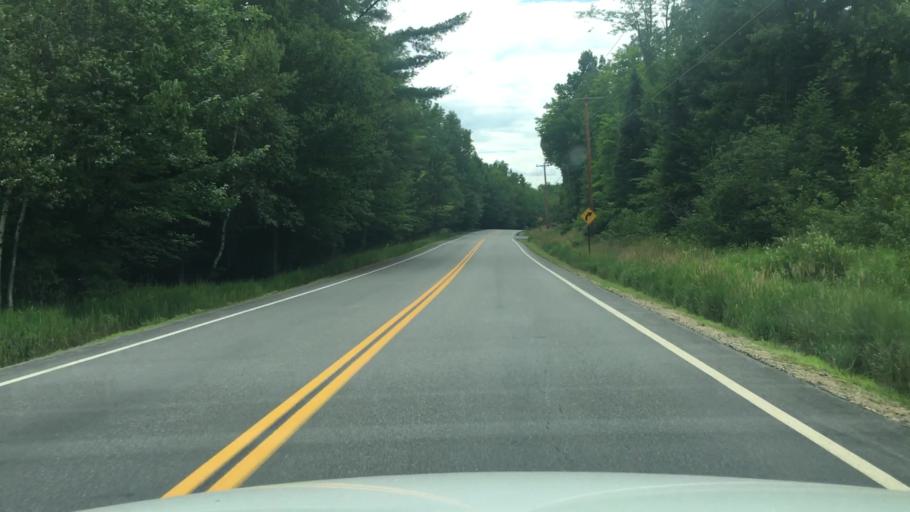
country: US
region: Maine
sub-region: Oxford County
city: West Paris
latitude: 44.3476
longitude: -70.5252
